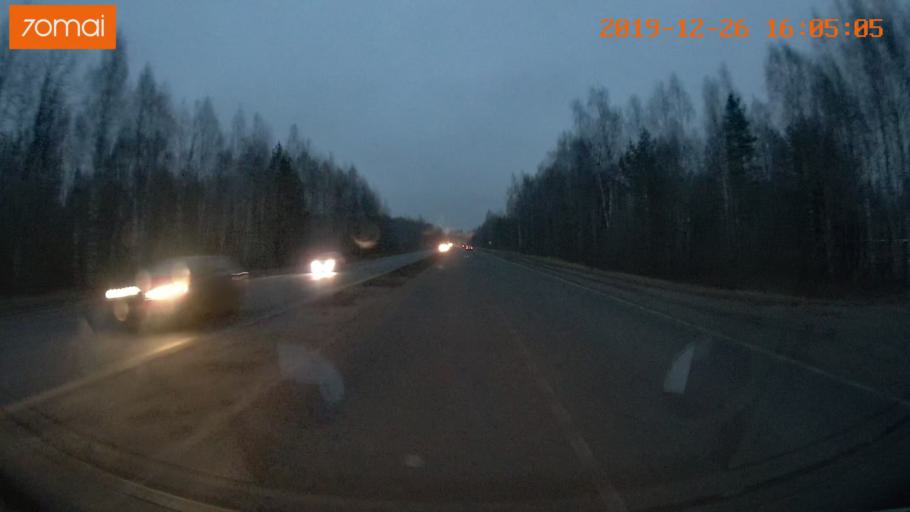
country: RU
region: Jaroslavl
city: Rybinsk
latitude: 58.0072
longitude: 38.8866
